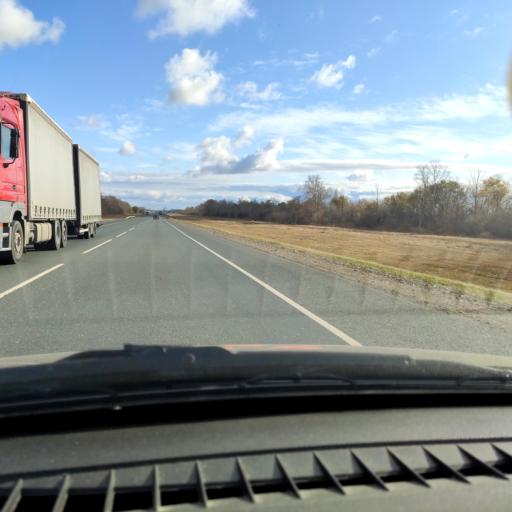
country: RU
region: Samara
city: Varlamovo
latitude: 53.1941
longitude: 48.2471
